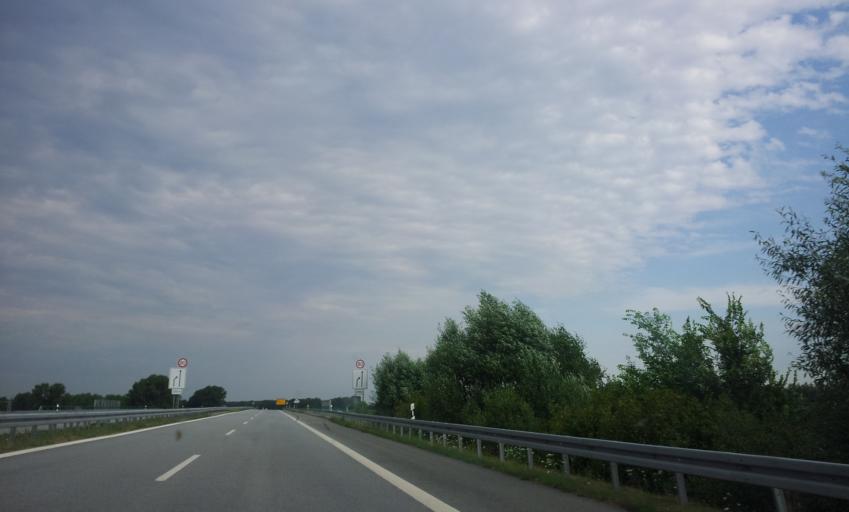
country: DE
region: Brandenburg
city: Trebbin
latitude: 52.2279
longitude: 13.2410
